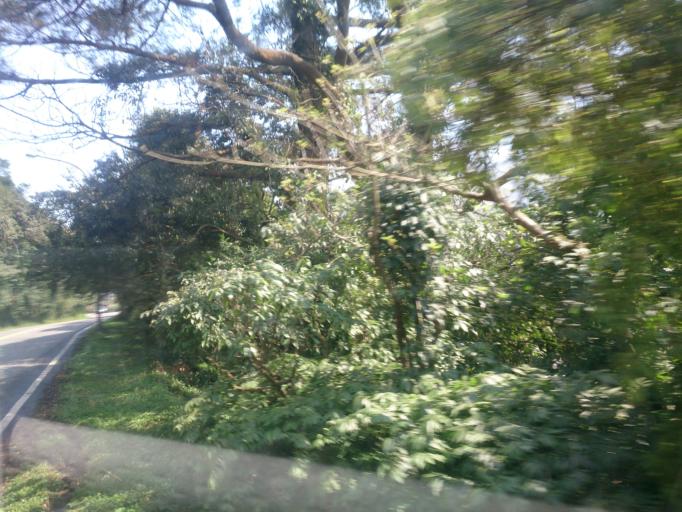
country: TW
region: Taipei
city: Taipei
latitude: 25.1800
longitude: 121.5427
